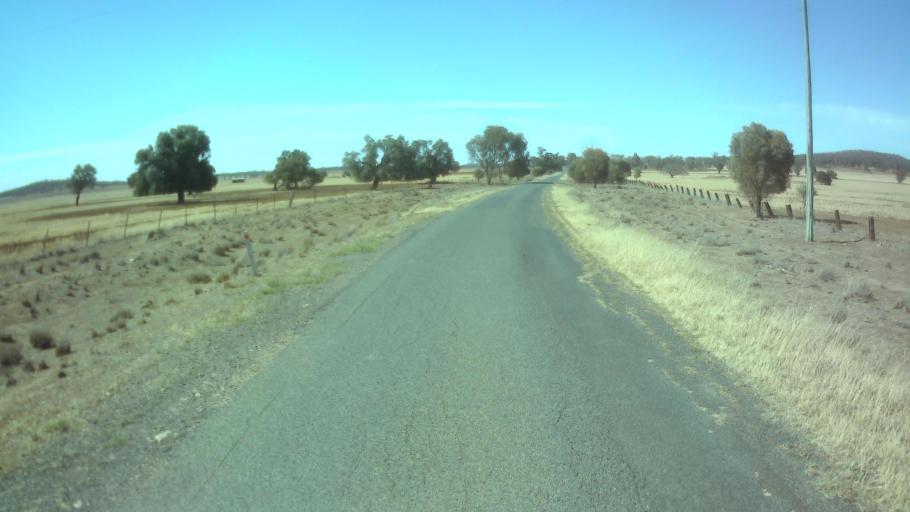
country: AU
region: New South Wales
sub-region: Forbes
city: Forbes
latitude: -33.7421
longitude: 147.7404
